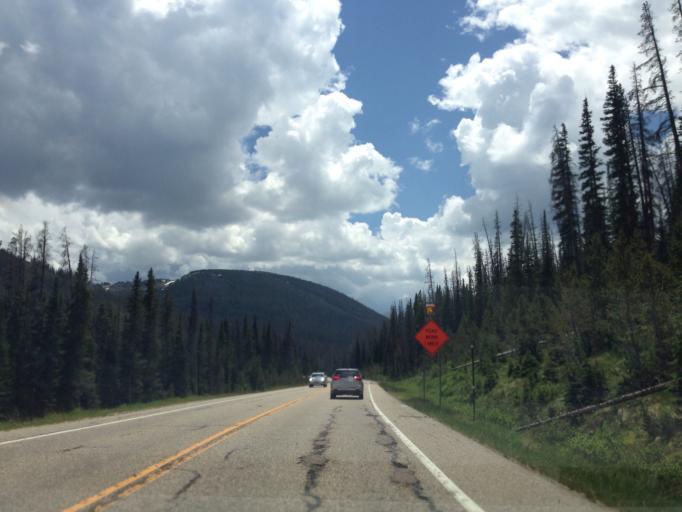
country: US
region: Colorado
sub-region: Larimer County
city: Estes Park
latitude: 40.5479
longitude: -105.8788
